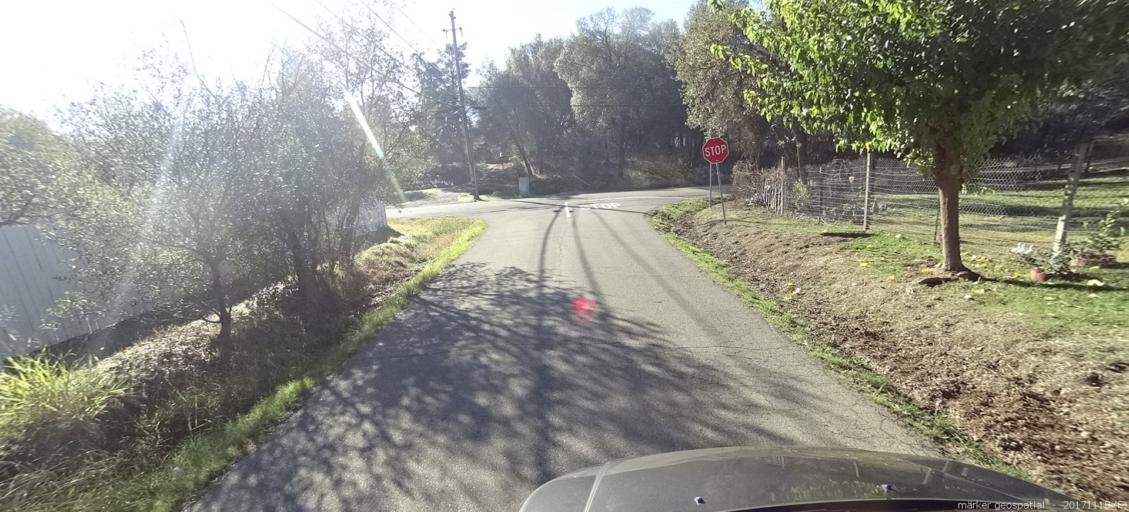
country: US
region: California
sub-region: Shasta County
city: Cottonwood
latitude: 40.3860
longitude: -122.3146
